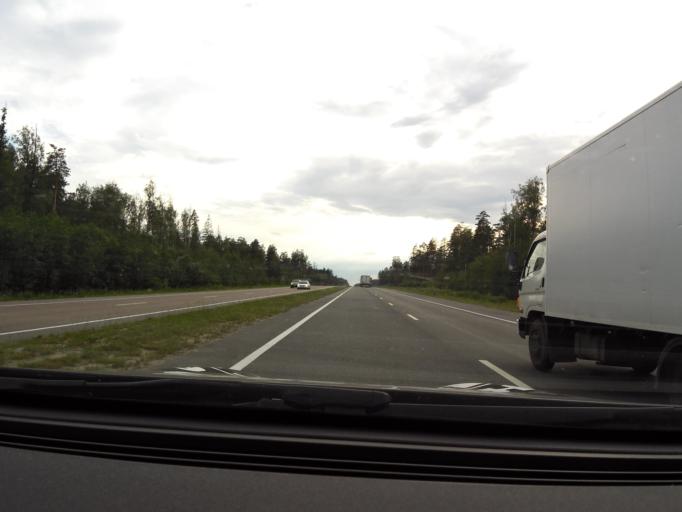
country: RU
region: Vladimir
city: Bogolyubovo
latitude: 56.0947
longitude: 40.5490
